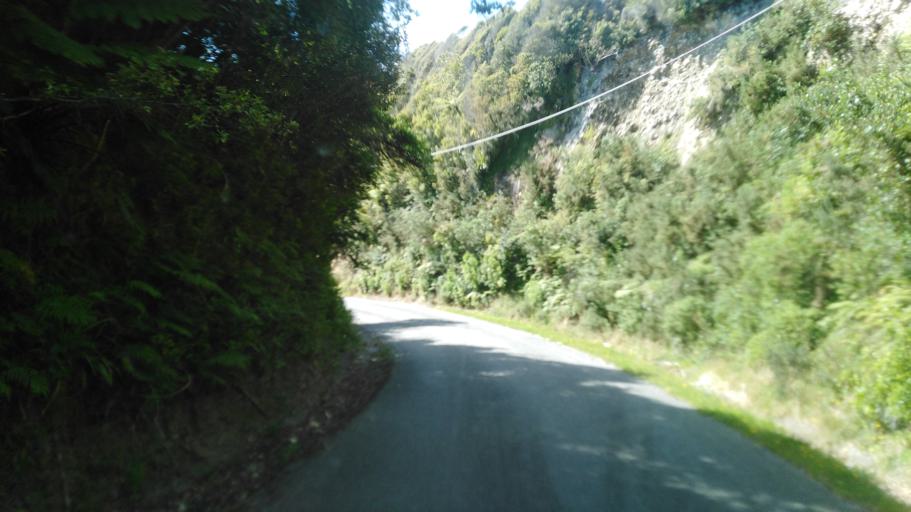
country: NZ
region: West Coast
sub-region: Buller District
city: Westport
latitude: -41.2614
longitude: 172.1131
